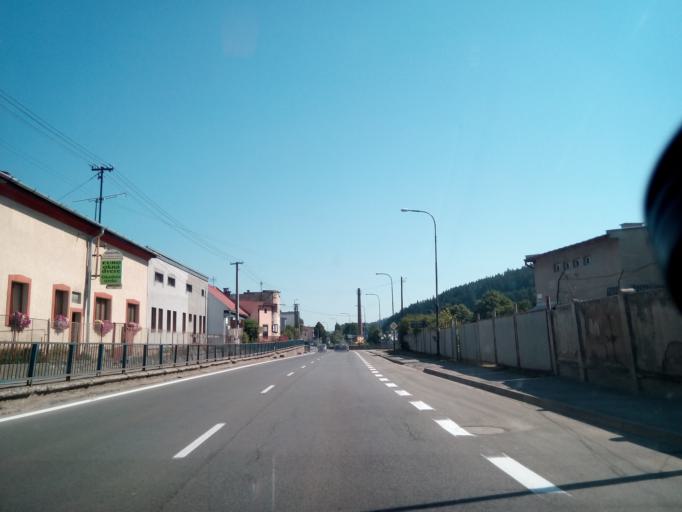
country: SK
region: Presovsky
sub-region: Okres Presov
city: Kezmarok
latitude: 49.1433
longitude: 20.4286
